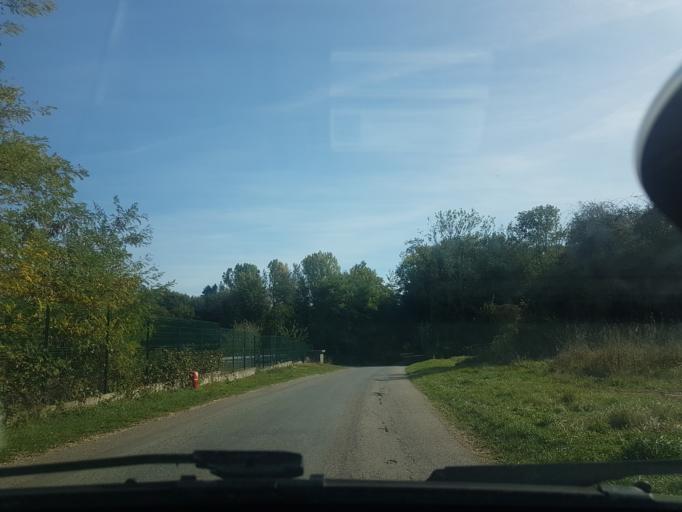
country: FR
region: Franche-Comte
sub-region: Territoire de Belfort
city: Chevremont
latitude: 47.6535
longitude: 6.9224
